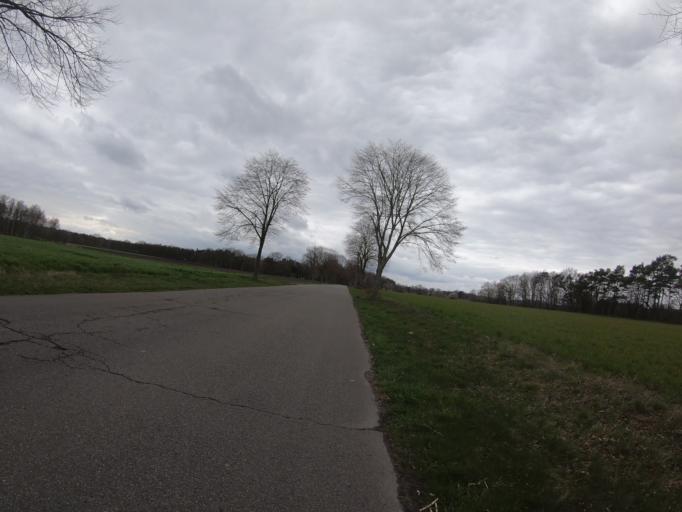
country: DE
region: Lower Saxony
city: Leiferde
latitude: 52.4978
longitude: 10.4302
